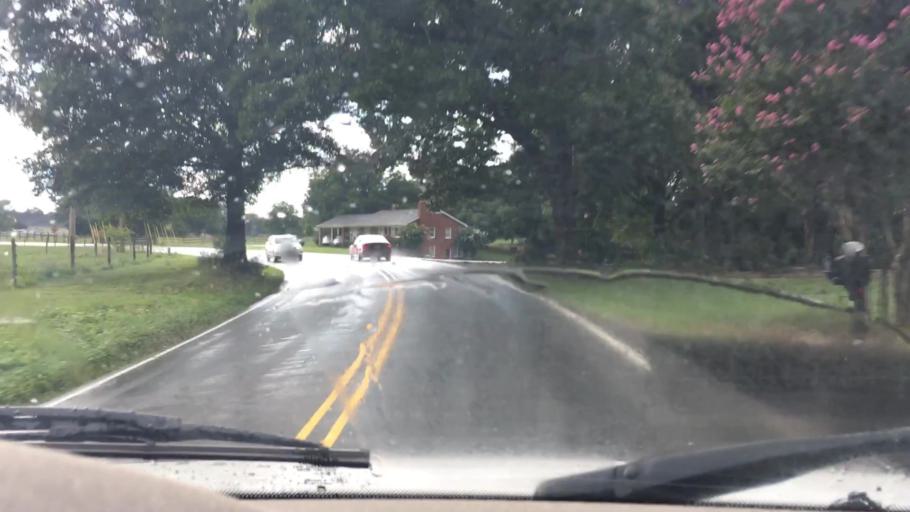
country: US
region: North Carolina
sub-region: Mecklenburg County
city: Huntersville
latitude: 35.4212
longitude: -80.9122
